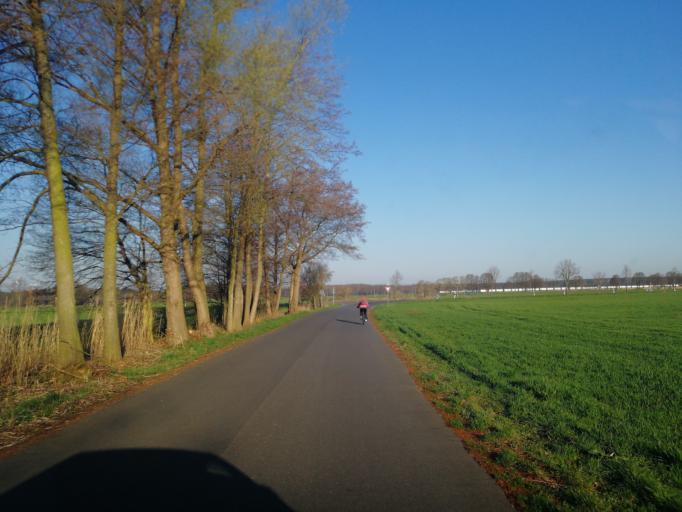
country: DE
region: Brandenburg
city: Drahnsdorf
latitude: 51.9271
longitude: 13.5967
